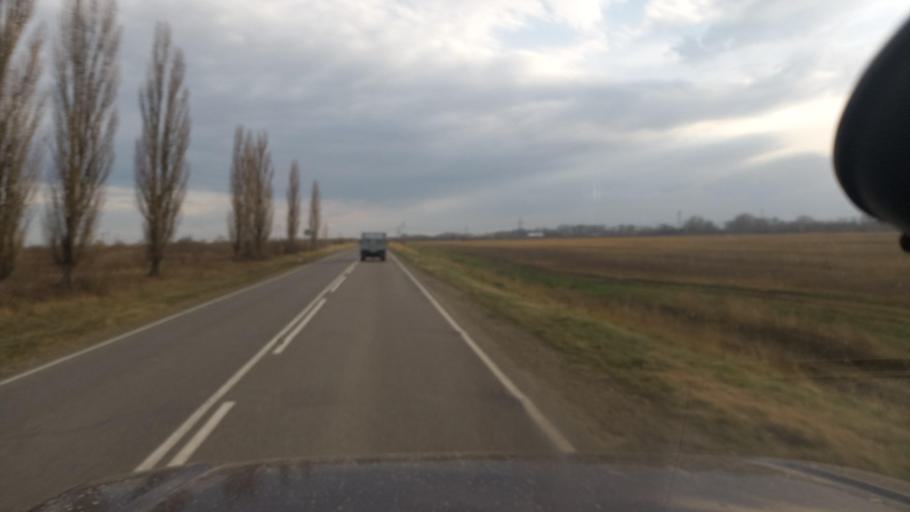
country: RU
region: Krasnodarskiy
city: Afipskiy
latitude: 44.8849
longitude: 38.8558
